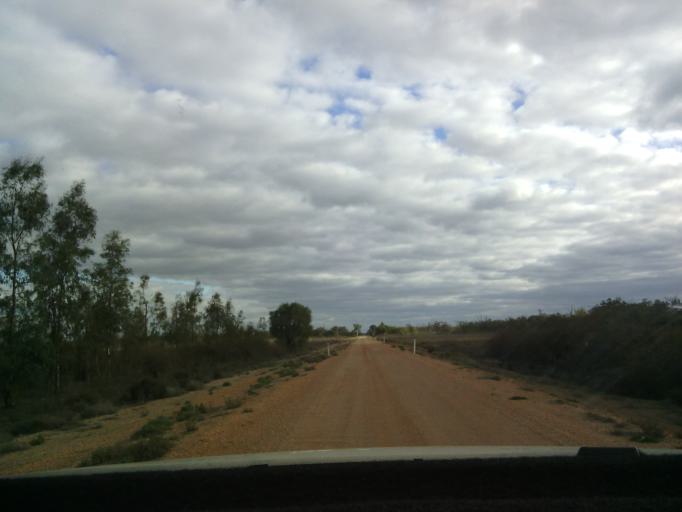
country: AU
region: South Australia
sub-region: Renmark Paringa
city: Renmark
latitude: -34.1636
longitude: 141.1971
